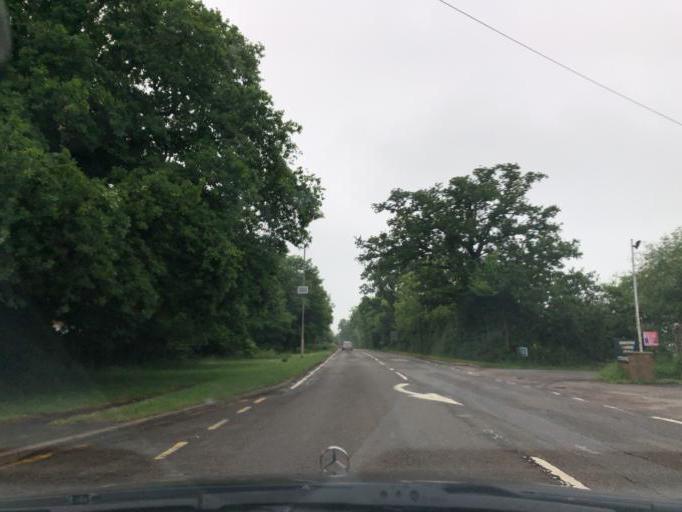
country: GB
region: England
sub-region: Warwickshire
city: Harbury
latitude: 52.2009
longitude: -1.4860
